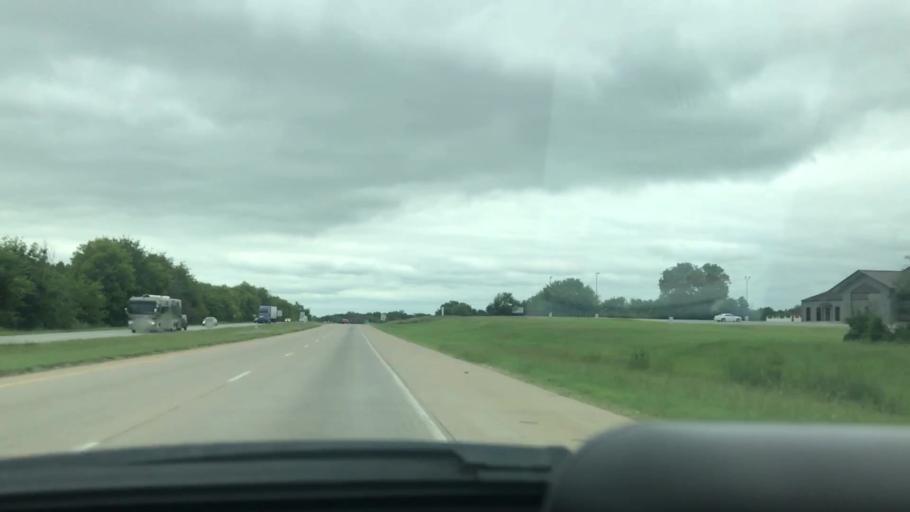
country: US
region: Oklahoma
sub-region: Mayes County
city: Chouteau
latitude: 36.1931
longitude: -95.3418
